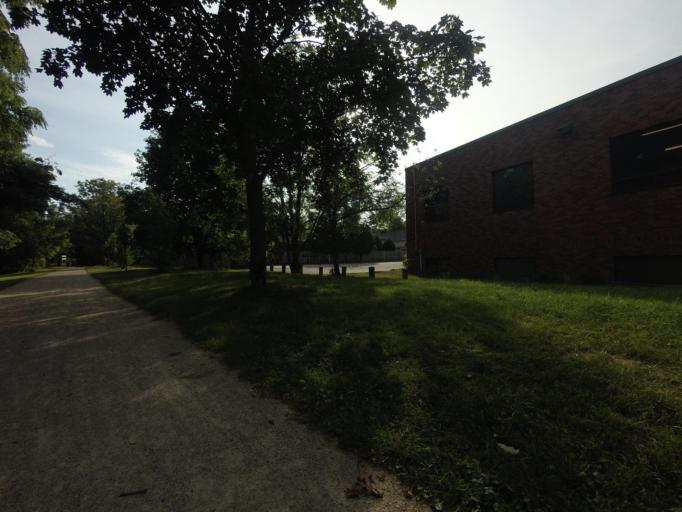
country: CA
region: Ontario
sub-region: Wellington County
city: Guelph
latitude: 43.5539
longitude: -80.2654
